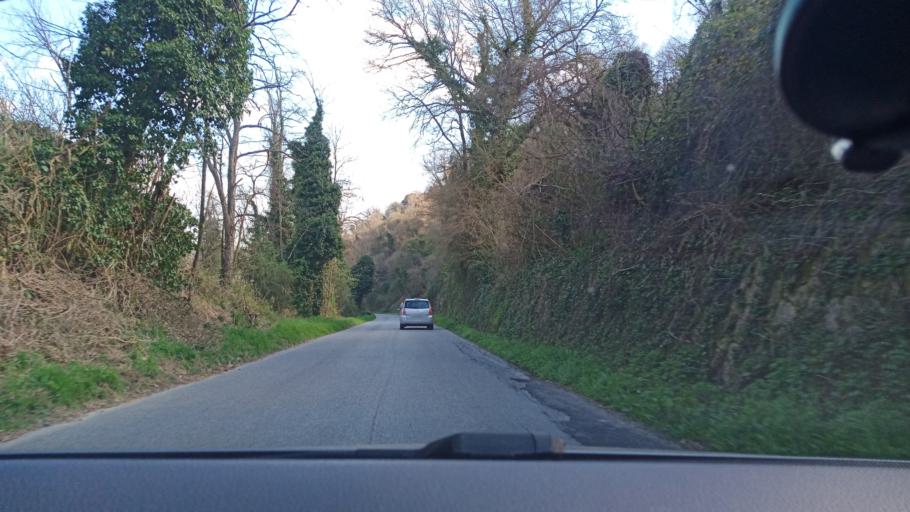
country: IT
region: Latium
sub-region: Citta metropolitana di Roma Capitale
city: Torrita Tiberina
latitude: 42.2383
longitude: 12.6241
